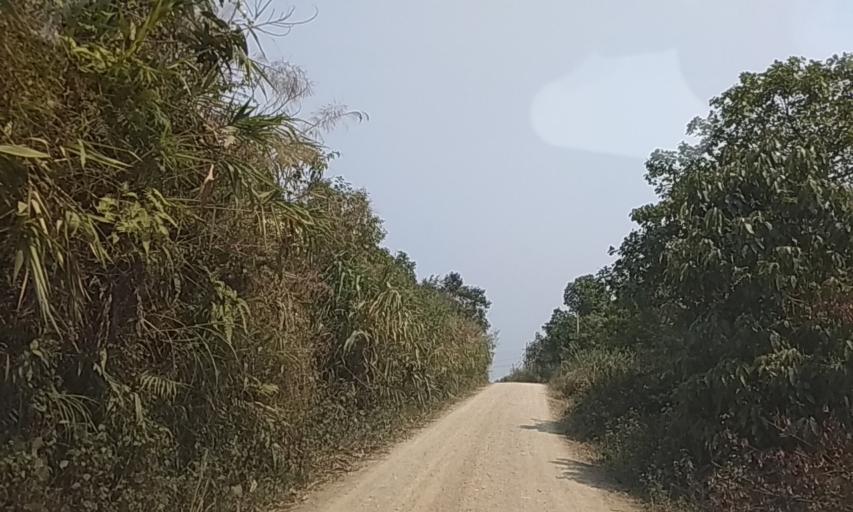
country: TH
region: Nan
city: Chaloem Phra Kiat
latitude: 20.0525
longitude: 101.0799
